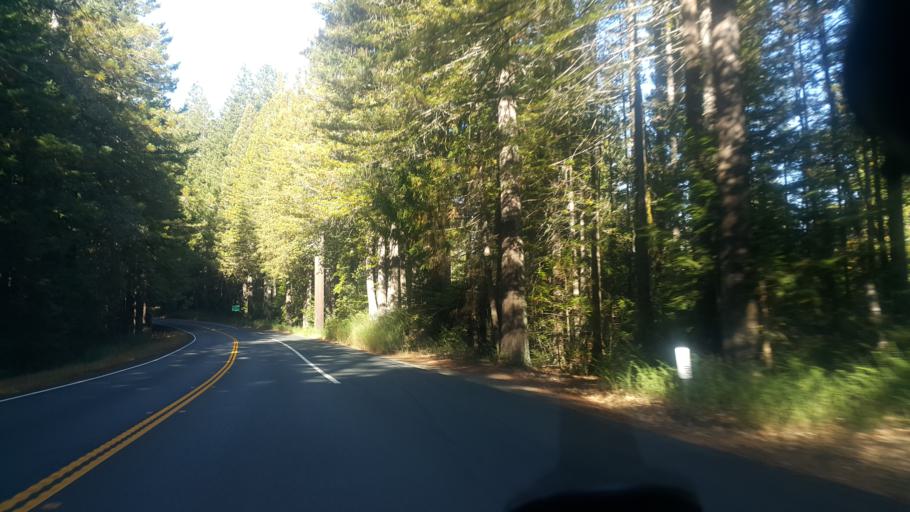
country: US
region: California
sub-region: Mendocino County
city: Fort Bragg
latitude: 39.3602
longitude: -123.6443
